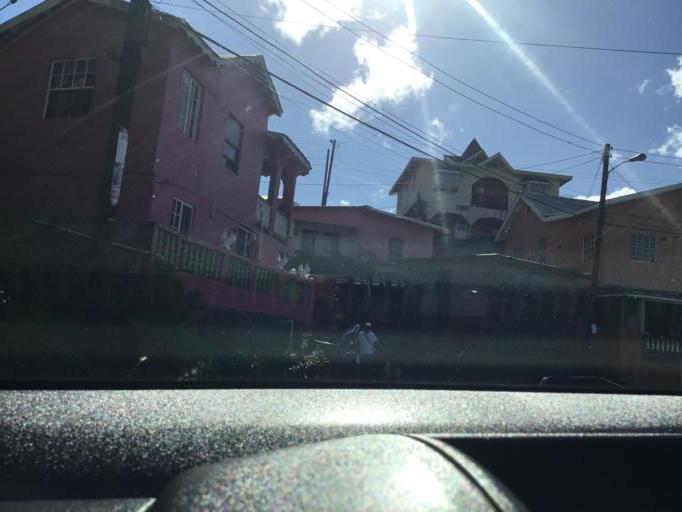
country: VC
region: Saint David
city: Chateaubelair
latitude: 13.2696
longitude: -61.2397
